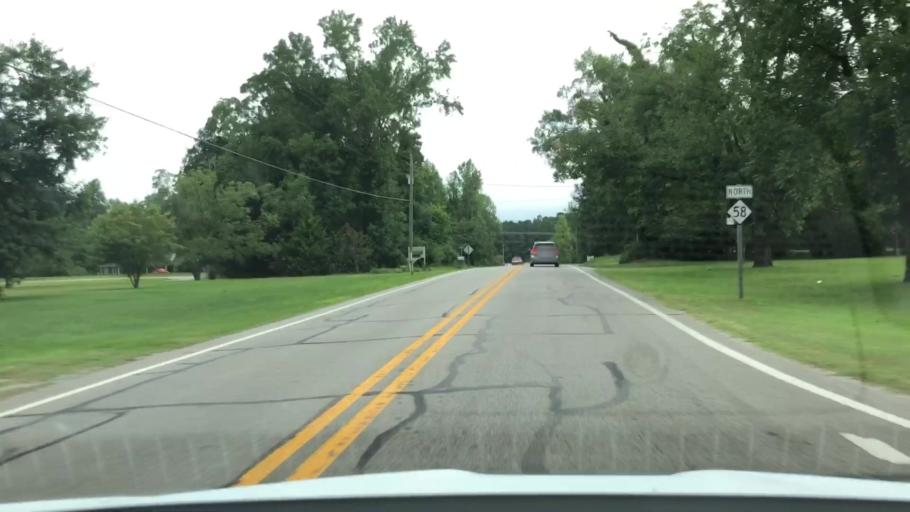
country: US
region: North Carolina
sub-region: Lenoir County
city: Kinston
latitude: 35.2152
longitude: -77.5704
